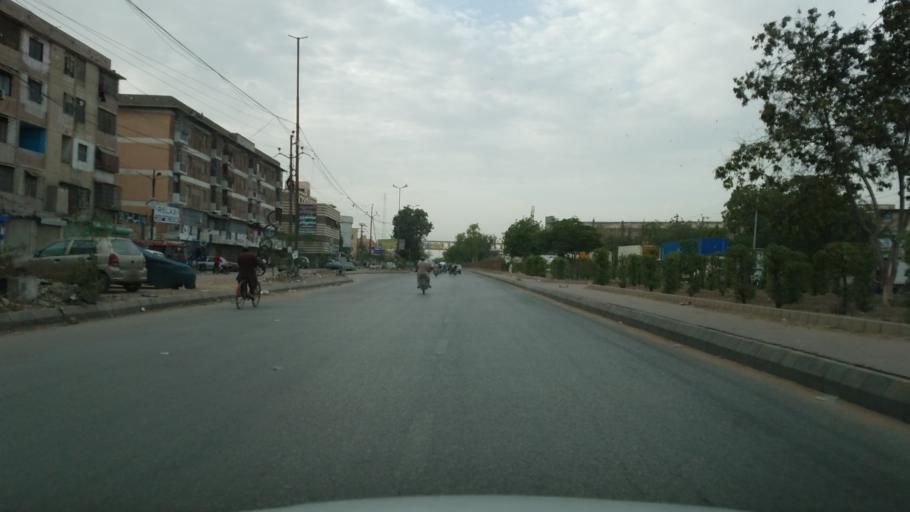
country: PK
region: Sindh
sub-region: Karachi District
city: Karachi
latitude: 24.9480
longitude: 67.0823
